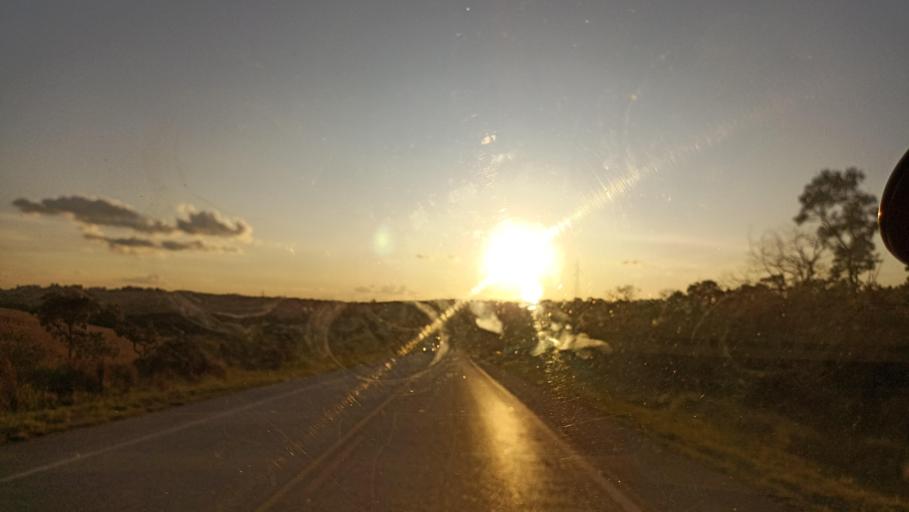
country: BR
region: Minas Gerais
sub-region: Sao Joao Del Rei
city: Sao Joao del Rei
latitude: -21.2256
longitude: -44.3690
